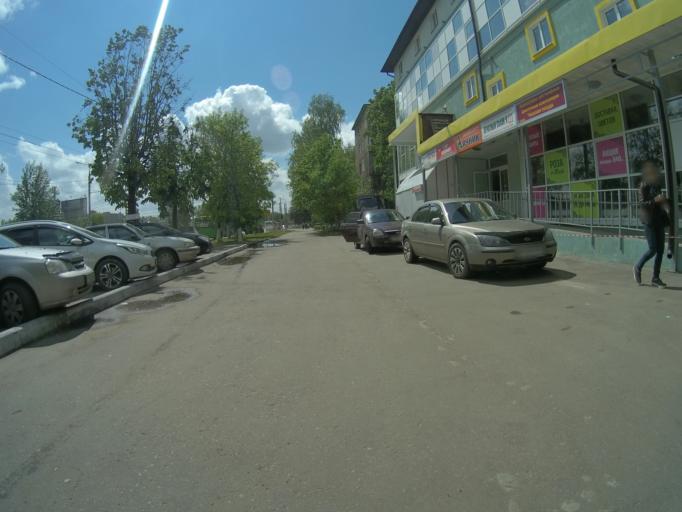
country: RU
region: Vladimir
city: Vladimir
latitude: 56.1426
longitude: 40.3673
